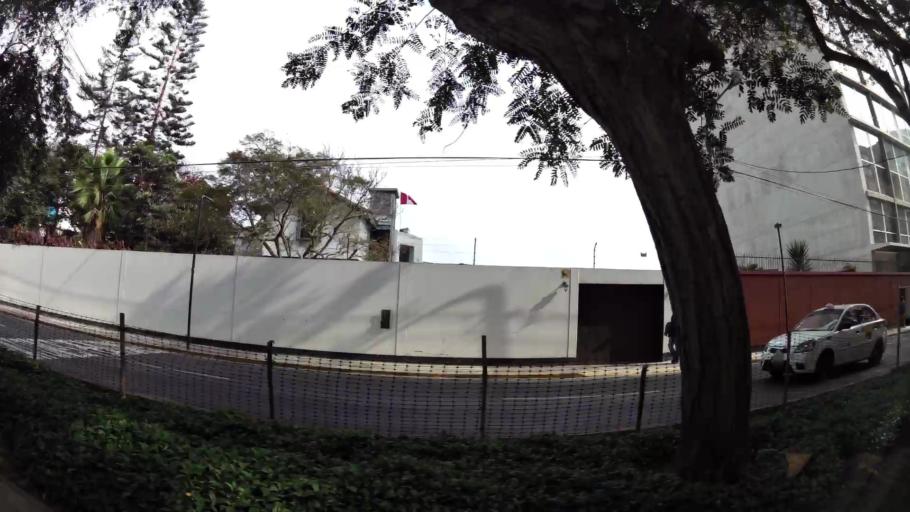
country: PE
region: Lima
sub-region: Lima
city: San Isidro
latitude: -12.0973
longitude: -77.0572
